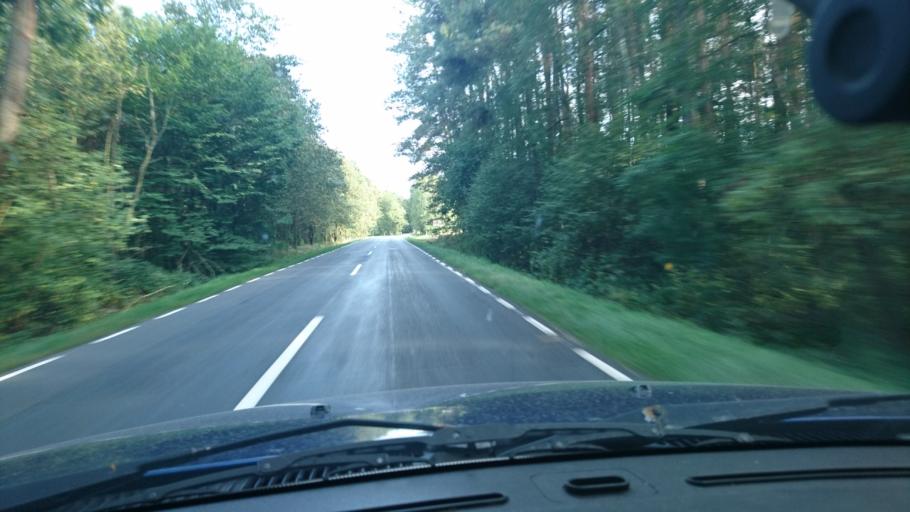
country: PL
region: Greater Poland Voivodeship
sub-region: Powiat krotoszynski
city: Sulmierzyce
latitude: 51.6284
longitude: 17.4959
